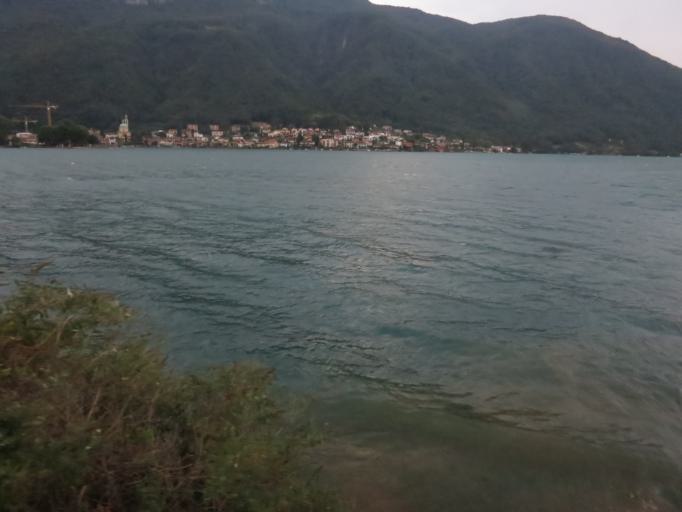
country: CH
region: Ticino
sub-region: Mendrisio District
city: Riva San Vitale
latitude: 45.9080
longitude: 8.9823
